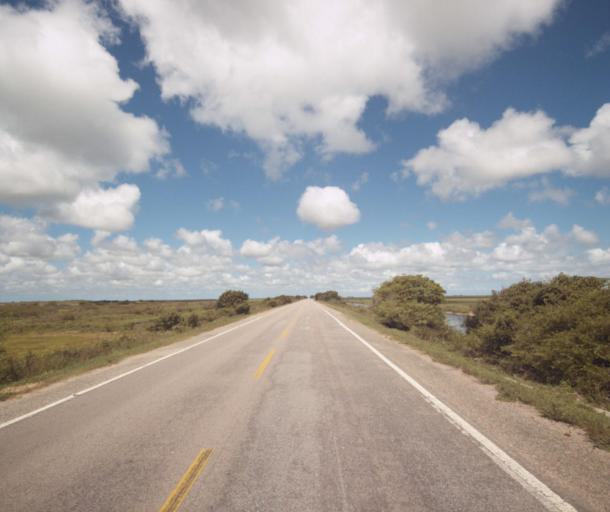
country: BR
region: Rio Grande do Sul
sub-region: Arroio Grande
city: Arroio Grande
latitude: -32.5421
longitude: -52.5406
